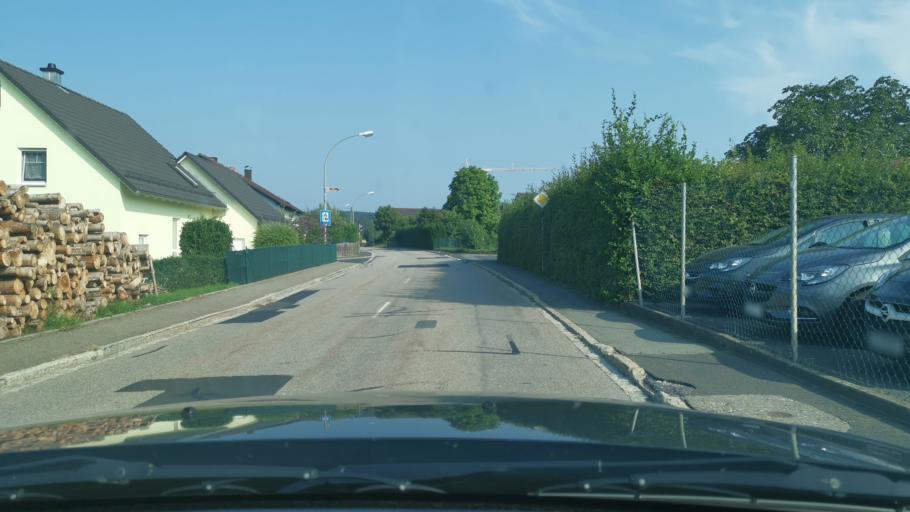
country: DE
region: Bavaria
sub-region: Upper Palatinate
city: Schnaittenbach
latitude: 49.5539
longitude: 12.0042
